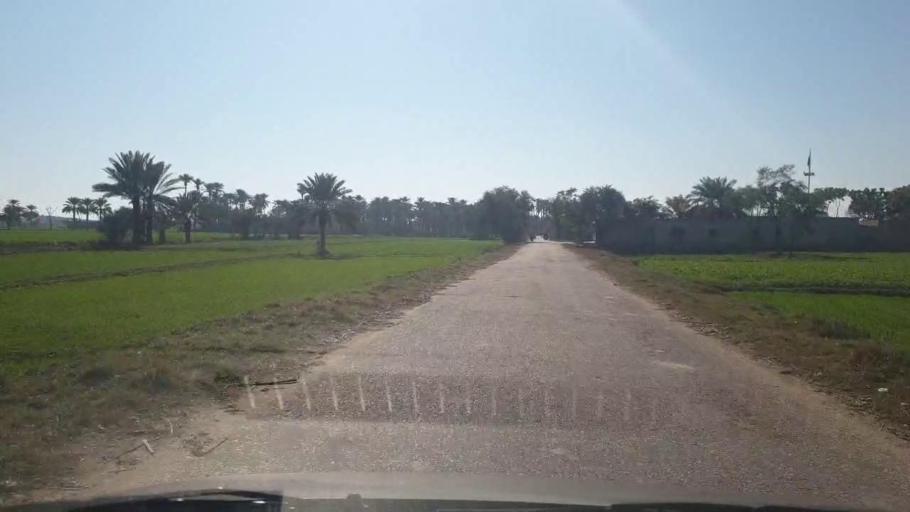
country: PK
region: Sindh
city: Bozdar
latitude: 27.1407
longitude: 68.6451
